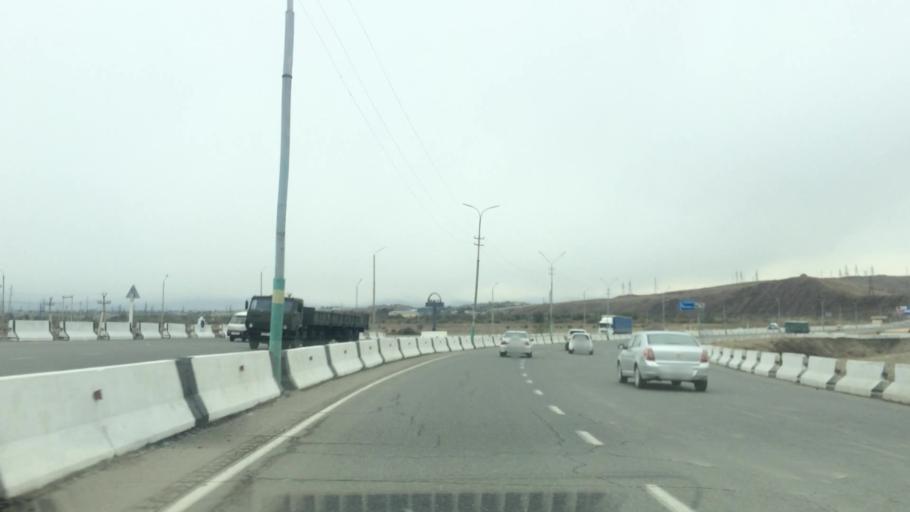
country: UZ
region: Samarqand
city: Jomboy
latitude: 39.6918
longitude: 67.0671
